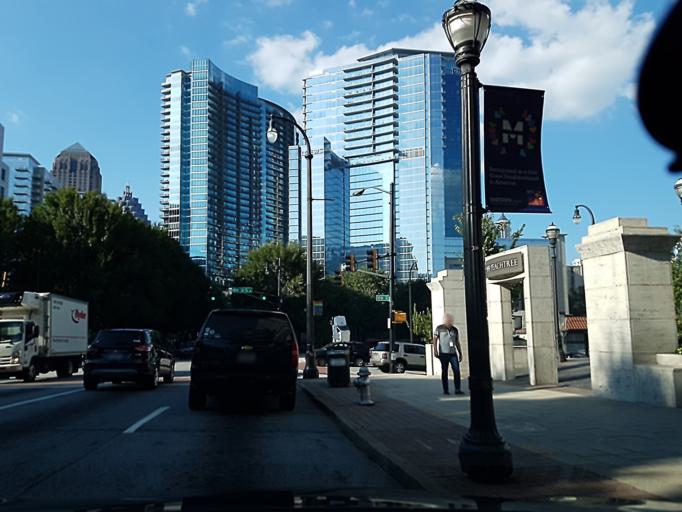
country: US
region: Georgia
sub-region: Fulton County
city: Atlanta
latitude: 33.7812
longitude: -84.3844
